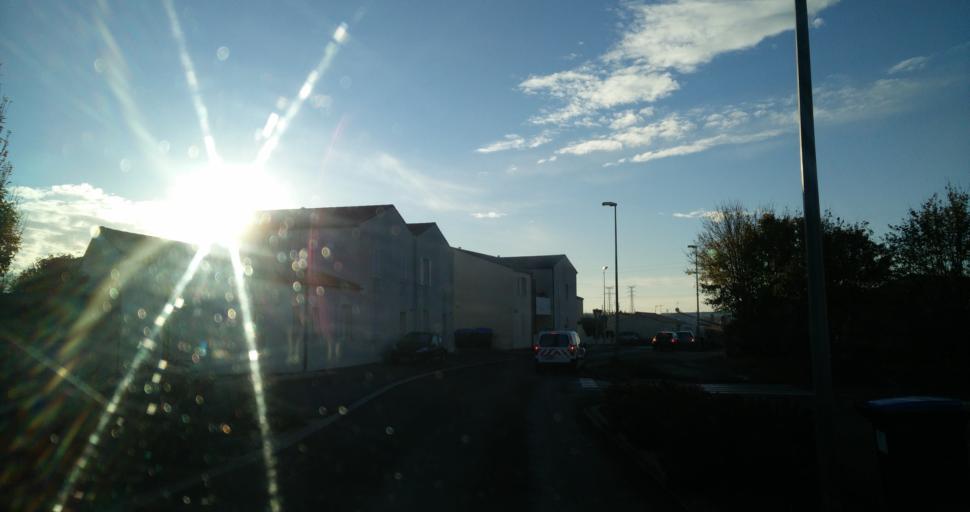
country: FR
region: Poitou-Charentes
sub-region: Departement de la Charente-Maritime
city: Puilboreau
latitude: 46.1832
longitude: -1.1256
